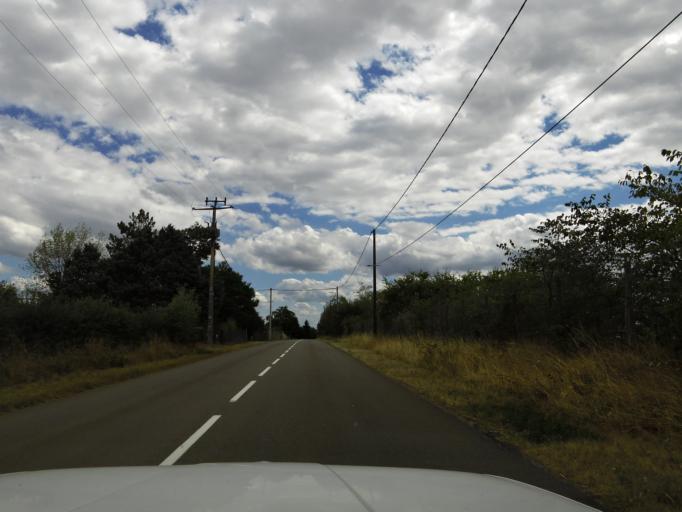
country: FR
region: Rhone-Alpes
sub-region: Departement de l'Ain
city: Meximieux
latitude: 45.8928
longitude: 5.2049
